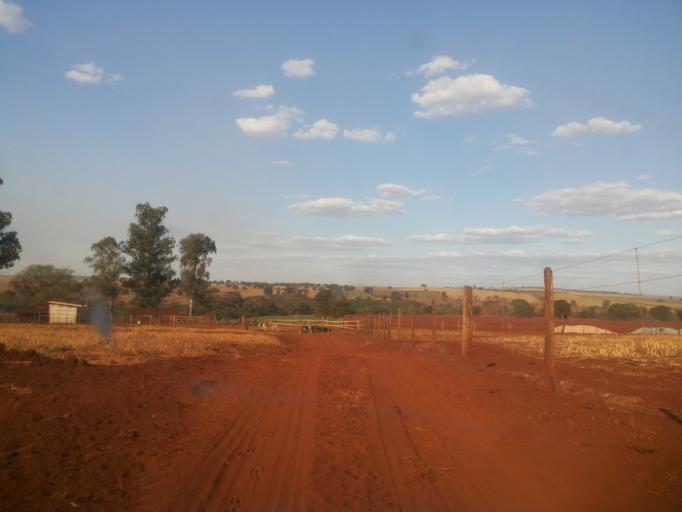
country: BR
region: Minas Gerais
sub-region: Capinopolis
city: Capinopolis
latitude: -18.6842
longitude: -49.3778
